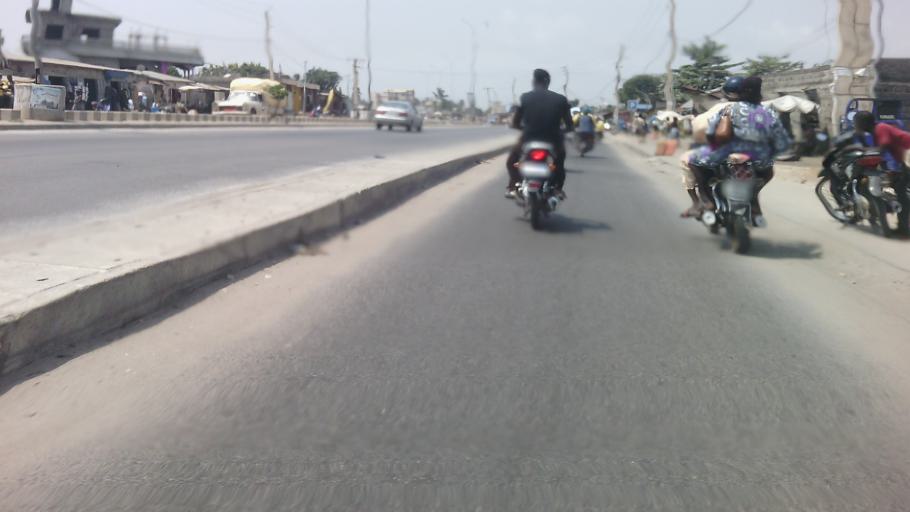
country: BJ
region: Atlantique
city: Abomey-Calavi
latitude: 6.3927
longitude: 2.3488
